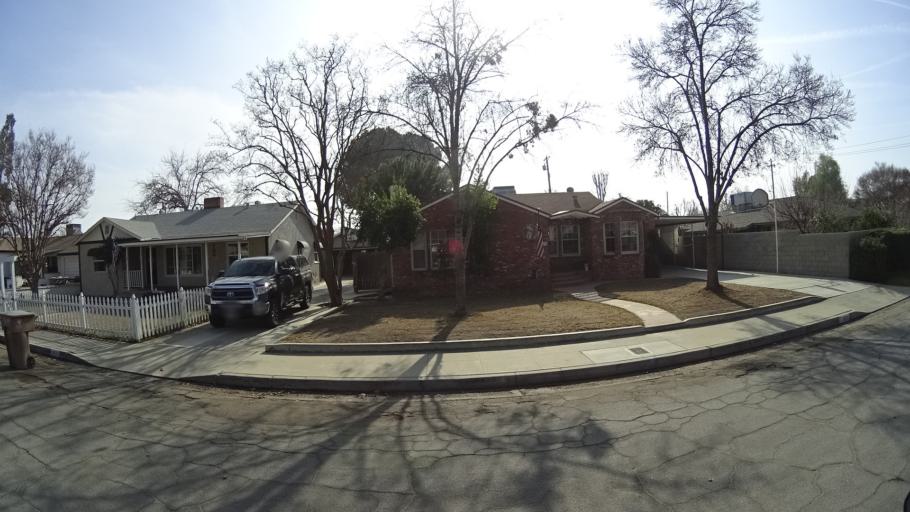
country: US
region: California
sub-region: Kern County
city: Bakersfield
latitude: 35.3590
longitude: -119.0312
